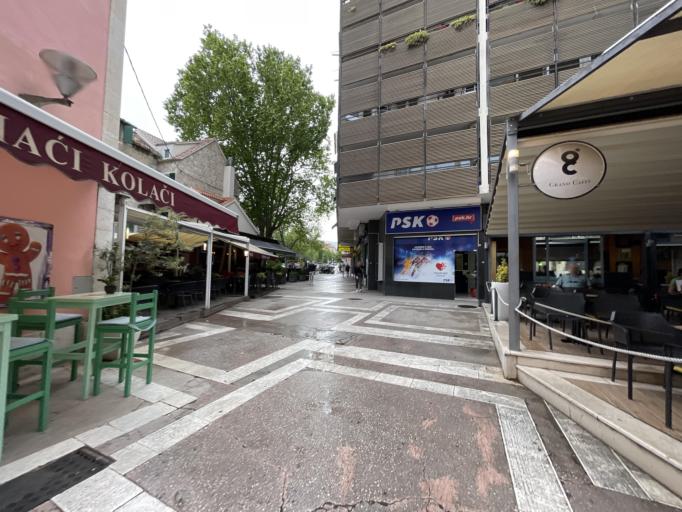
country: HR
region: Splitsko-Dalmatinska
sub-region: Grad Split
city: Split
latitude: 43.5114
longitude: 16.4364
